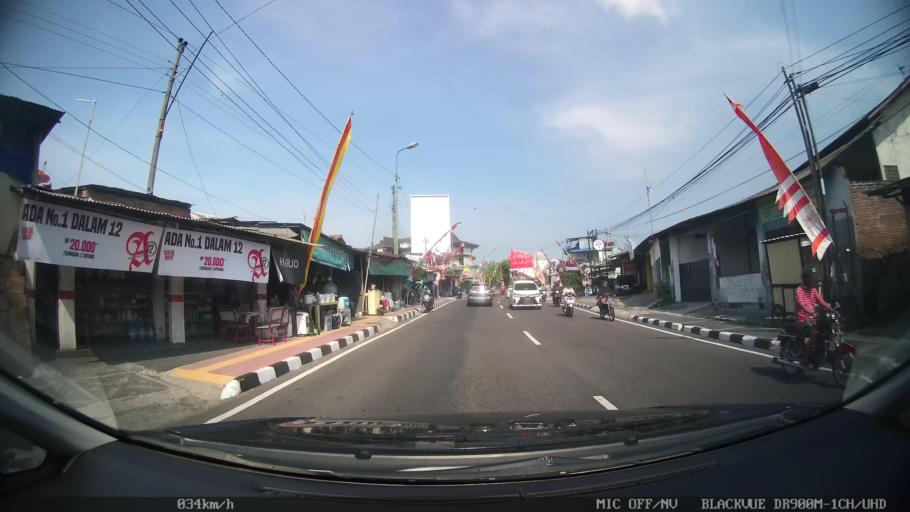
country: ID
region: Daerah Istimewa Yogyakarta
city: Yogyakarta
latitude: -7.7903
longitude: 110.3561
